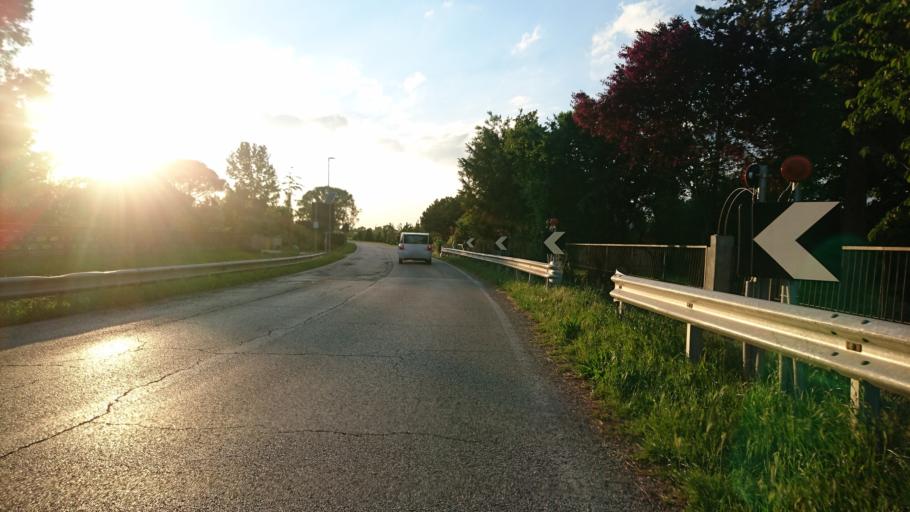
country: IT
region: Veneto
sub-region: Provincia di Rovigo
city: Castelmassa
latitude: 45.0227
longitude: 11.3033
